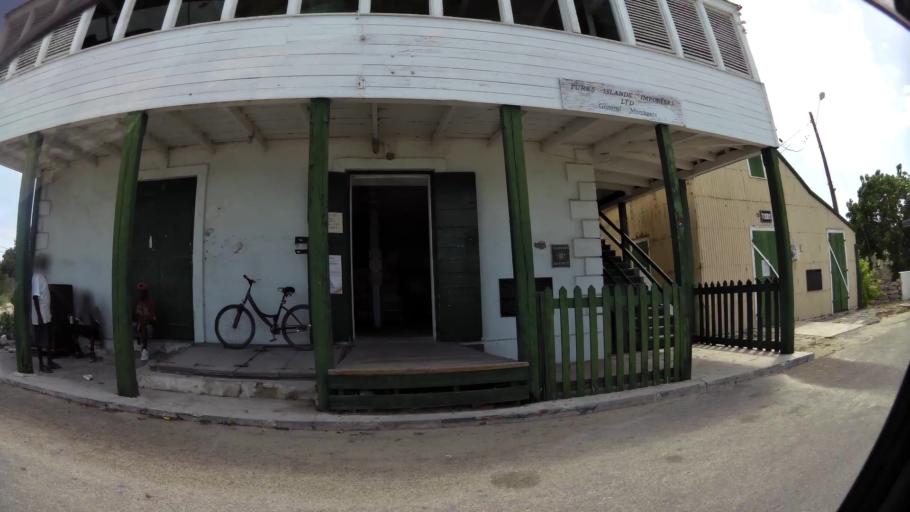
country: TC
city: Cockburn Town
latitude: 21.4702
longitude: -71.1471
